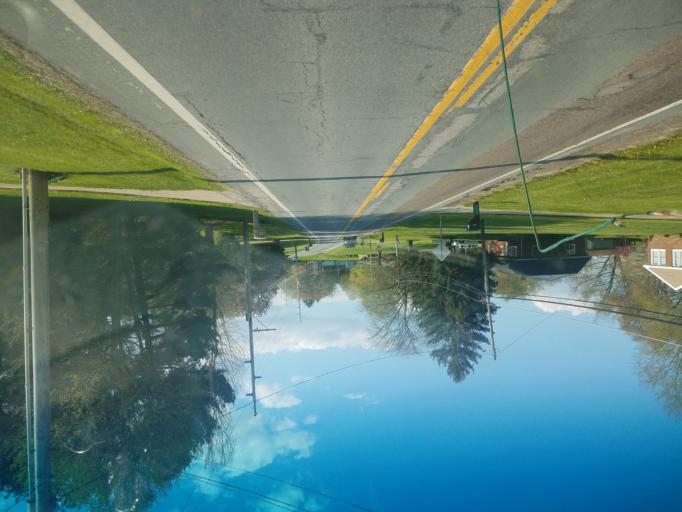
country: US
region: Ohio
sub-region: Wayne County
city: Shreve
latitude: 40.7178
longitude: -81.9439
